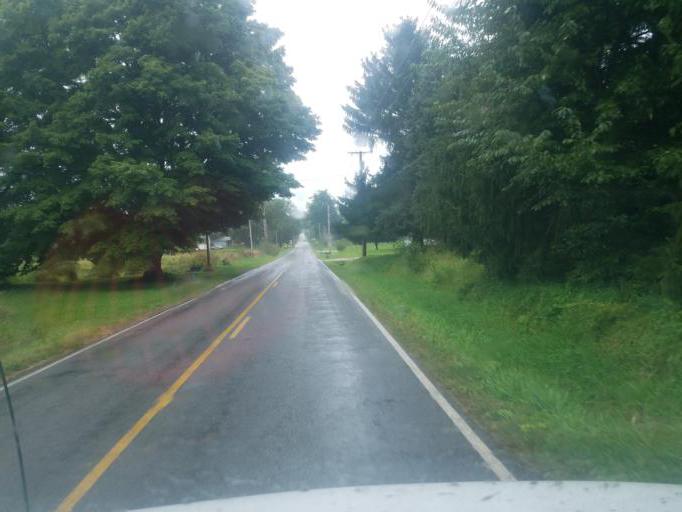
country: US
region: Ohio
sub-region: Medina County
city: Seville
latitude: 41.0100
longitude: -81.8505
